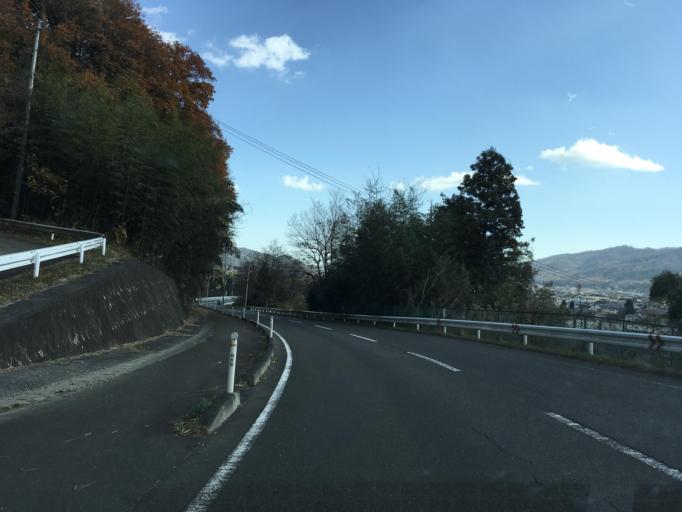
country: JP
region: Miyagi
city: Sendai
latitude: 38.2800
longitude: 140.7597
